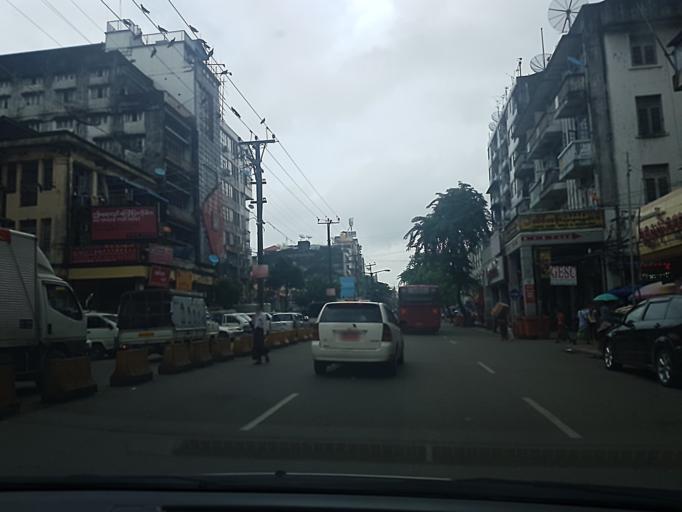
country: MM
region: Yangon
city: Yangon
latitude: 16.7748
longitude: 96.1492
